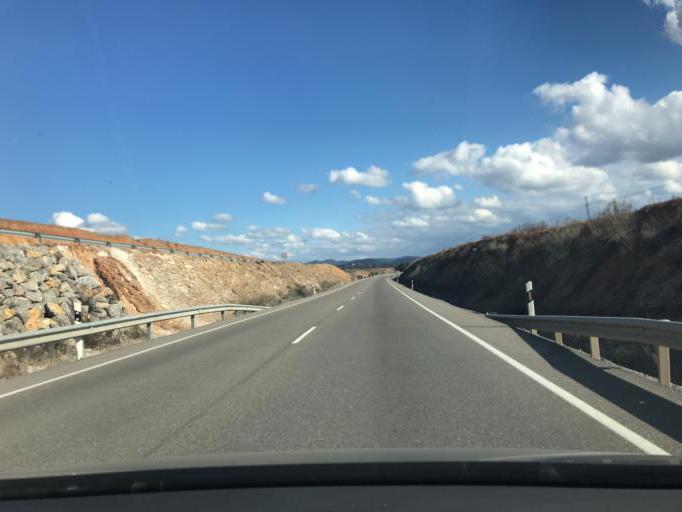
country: ES
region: Andalusia
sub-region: Province of Cordoba
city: Penarroya-Pueblonuevo
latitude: 38.2966
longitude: -5.2428
